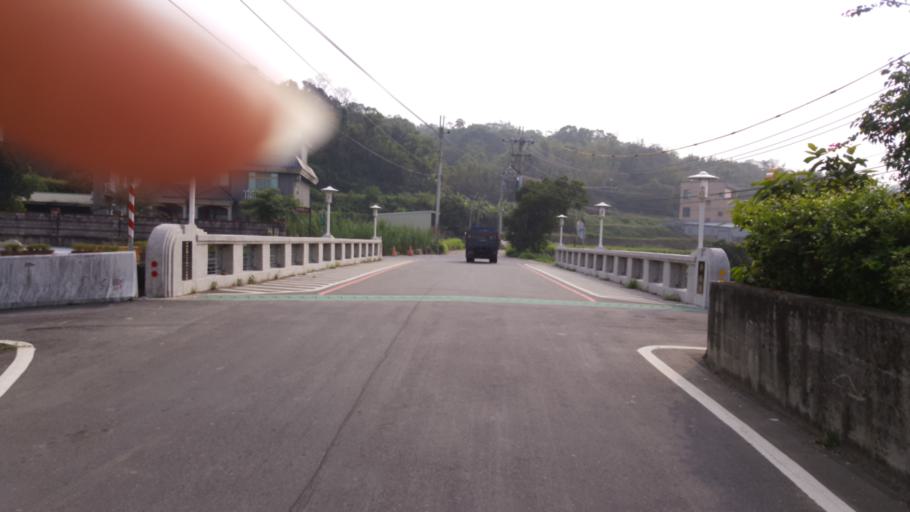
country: TW
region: Taiwan
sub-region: Hsinchu
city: Hsinchu
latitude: 24.7302
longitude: 120.9644
